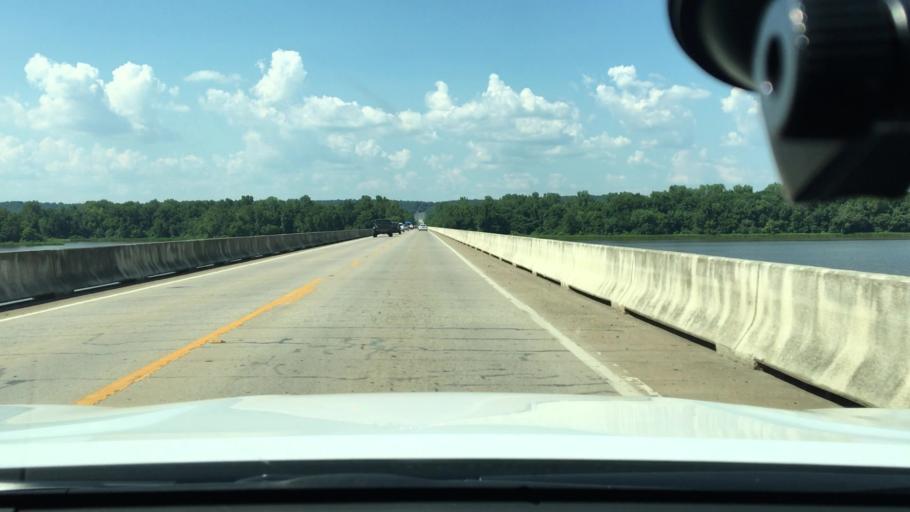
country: US
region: Arkansas
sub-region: Johnson County
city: Clarksville
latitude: 35.3907
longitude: -93.5302
